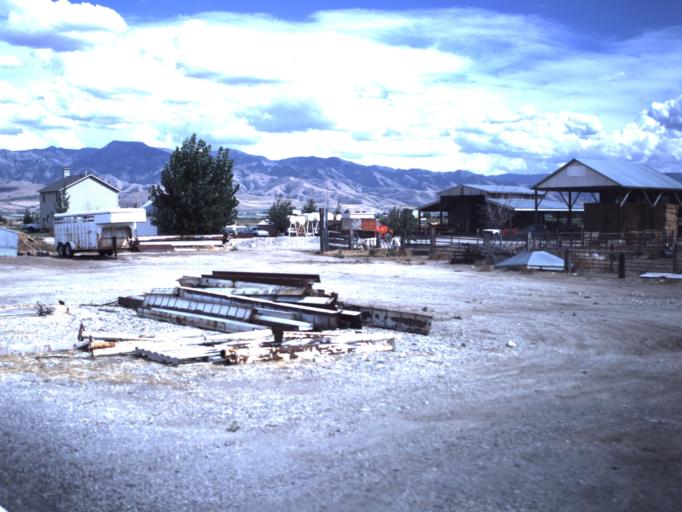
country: US
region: Utah
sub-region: Cache County
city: Lewiston
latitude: 41.9146
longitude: -111.9208
